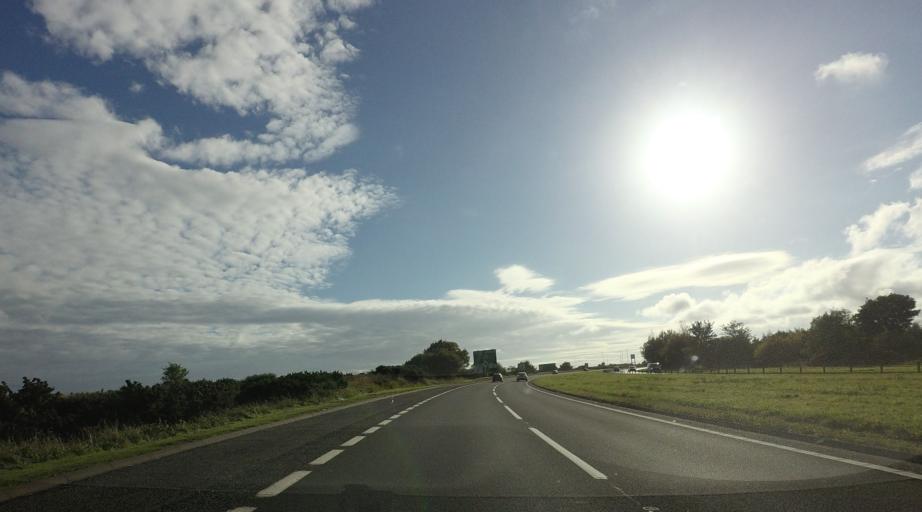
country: GB
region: Scotland
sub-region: Fife
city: Thornton
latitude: 56.1475
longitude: -3.1363
